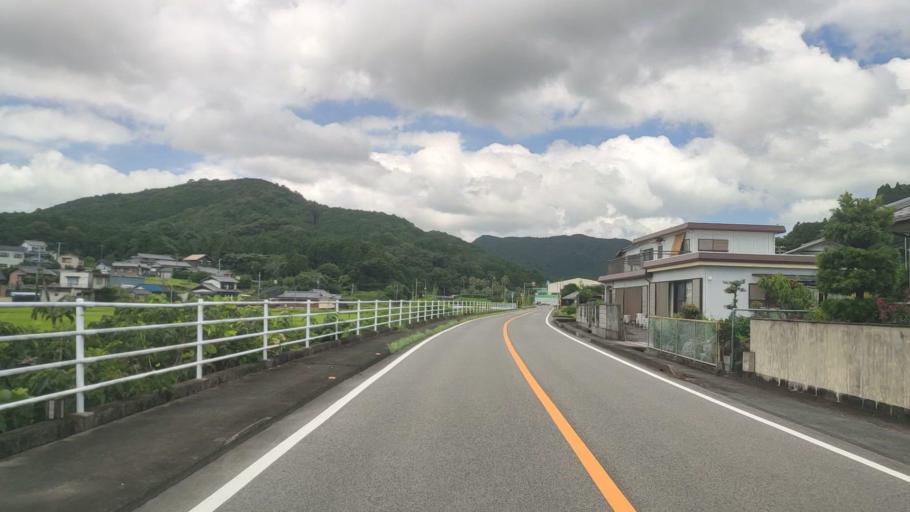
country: JP
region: Mie
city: Toba
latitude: 34.3852
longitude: 136.7996
